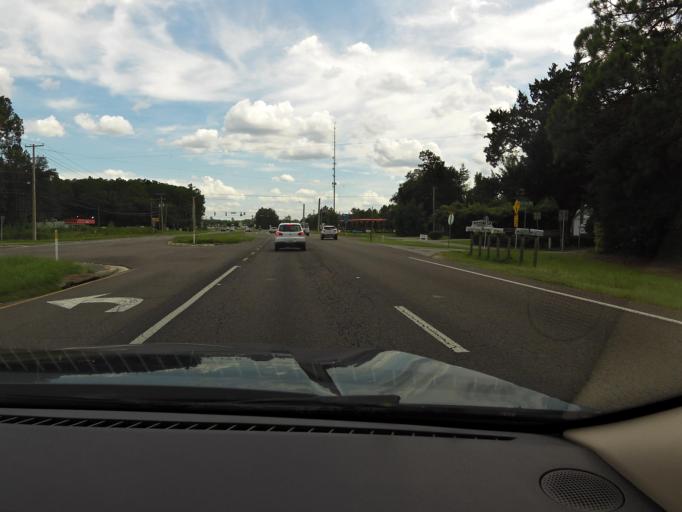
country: US
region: Florida
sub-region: Clay County
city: Green Cove Springs
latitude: 30.0327
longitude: -81.7103
